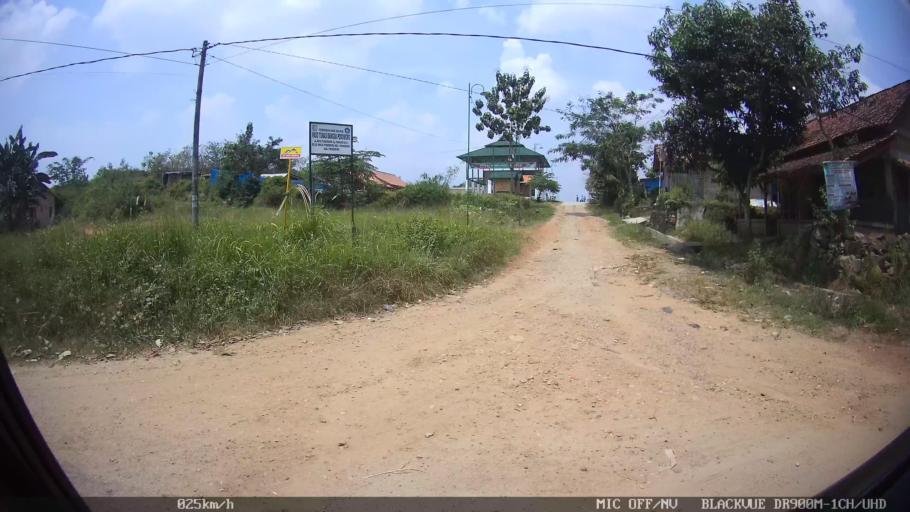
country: ID
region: Lampung
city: Pringsewu
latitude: -5.3416
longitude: 104.9850
